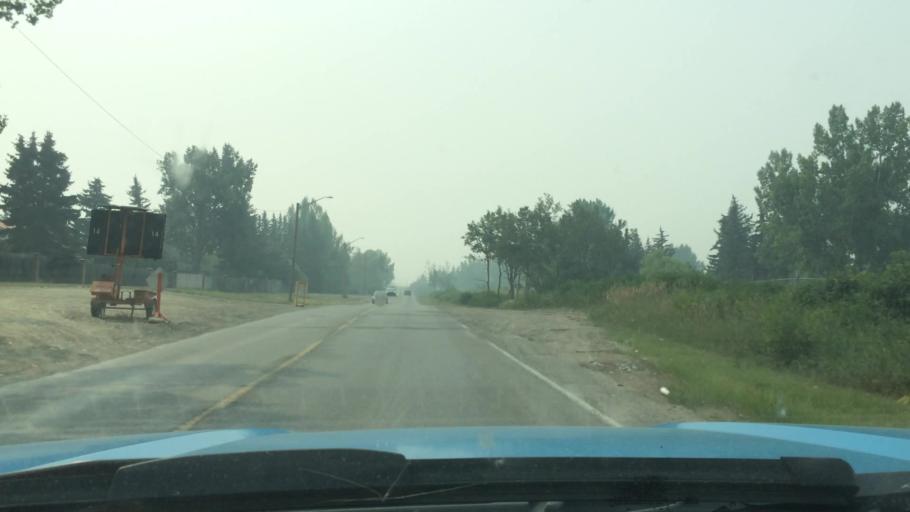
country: CA
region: Alberta
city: Calgary
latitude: 50.9477
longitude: -114.0948
